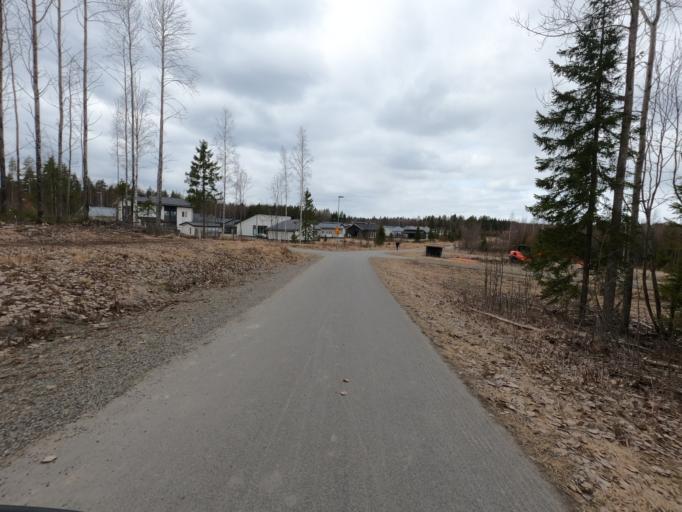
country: FI
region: North Karelia
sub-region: Joensuu
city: Joensuu
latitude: 62.5660
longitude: 29.8189
